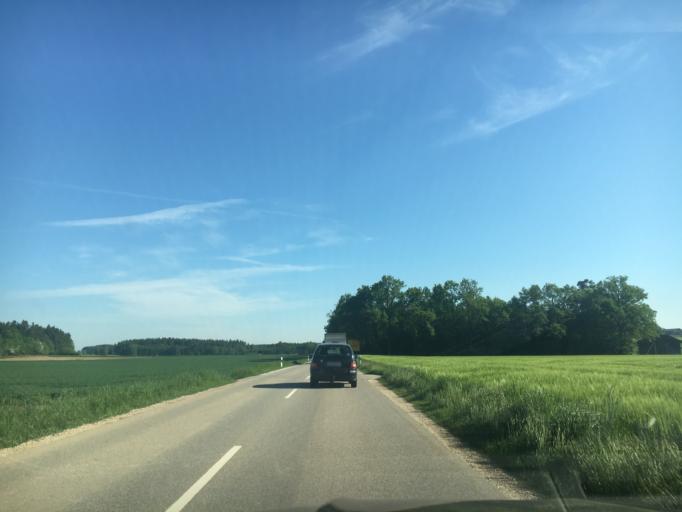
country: DE
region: Bavaria
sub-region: Upper Bavaria
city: Kirchweidach
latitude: 48.0520
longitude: 12.6166
